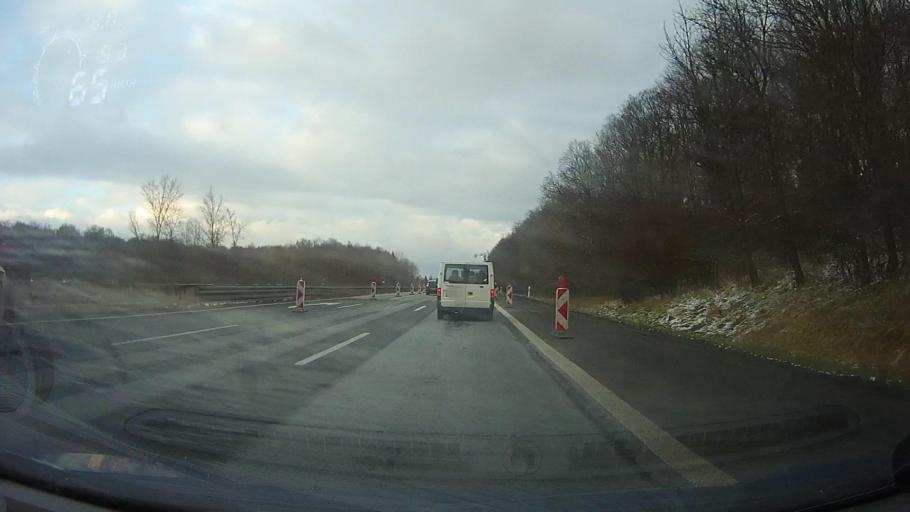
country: DE
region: Lower Saxony
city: Hillerse
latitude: 51.6699
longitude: 9.9214
